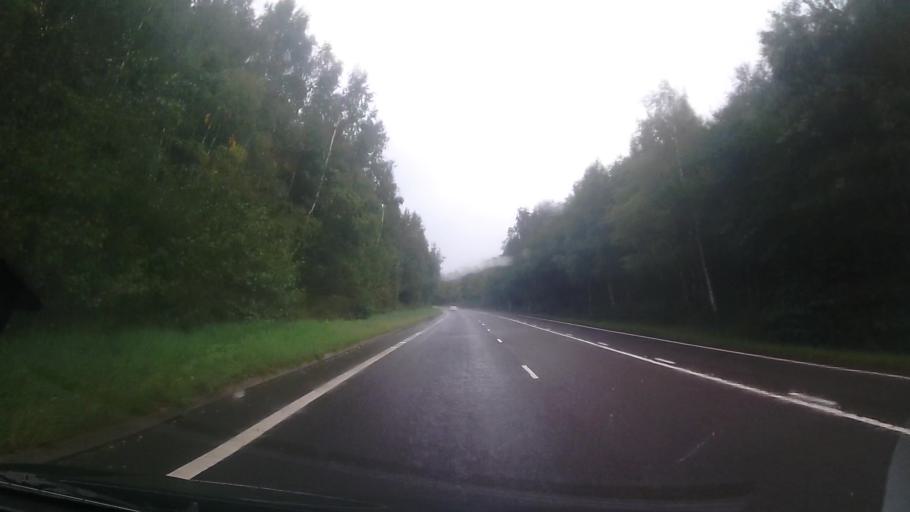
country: GB
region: England
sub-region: Telford and Wrekin
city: Ironbridge
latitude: 52.6434
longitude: -2.5114
